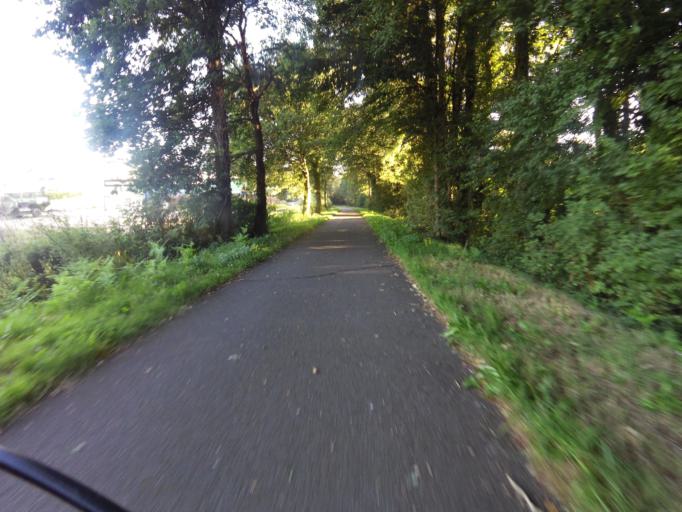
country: FR
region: Brittany
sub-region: Departement du Morbihan
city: Malestroit
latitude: 47.8289
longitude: -2.4197
